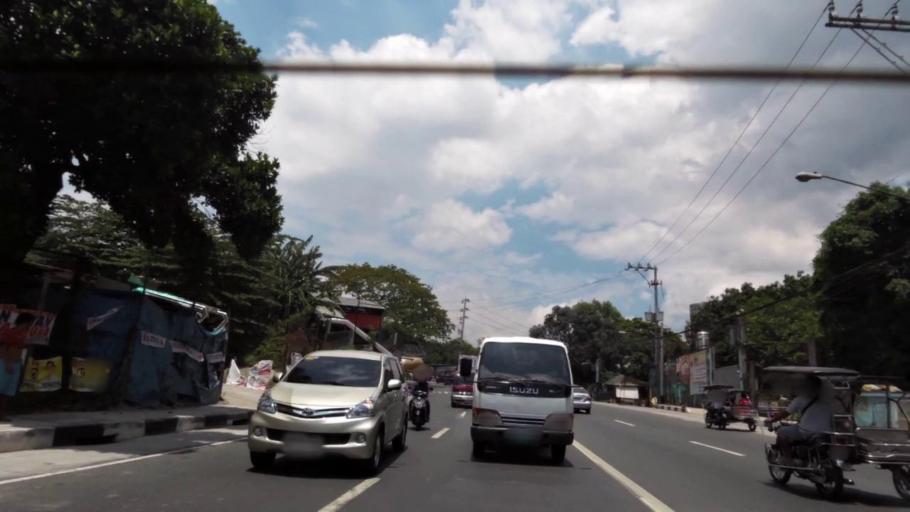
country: PH
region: Calabarzon
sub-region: Province of Rizal
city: Antipolo
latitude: 14.6057
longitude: 121.1737
